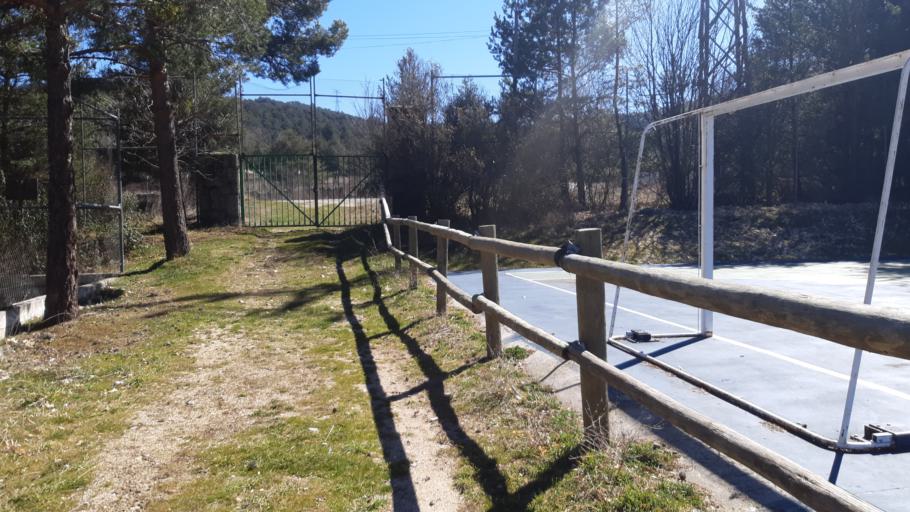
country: ES
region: Madrid
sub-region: Provincia de Madrid
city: Guadarrama
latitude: 40.7179
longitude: -4.1609
